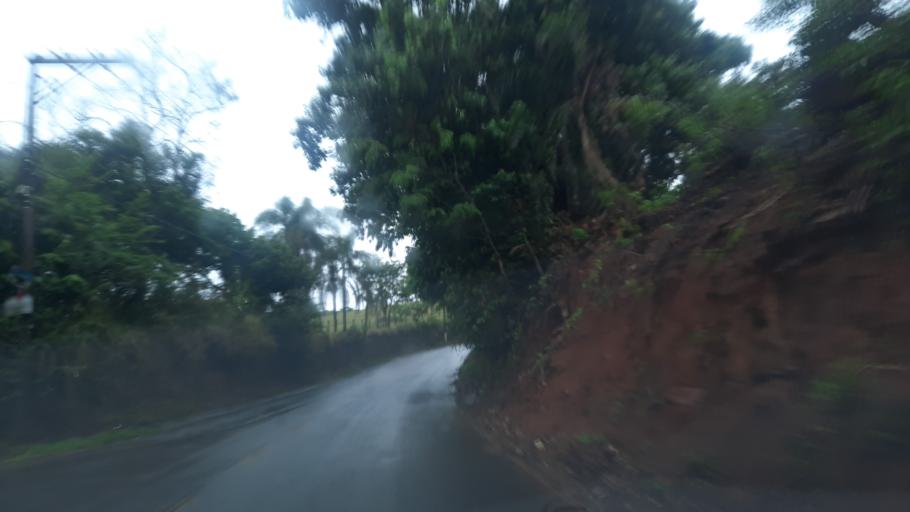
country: BR
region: Sao Paulo
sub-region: Atibaia
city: Atibaia
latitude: -23.0798
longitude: -46.5250
